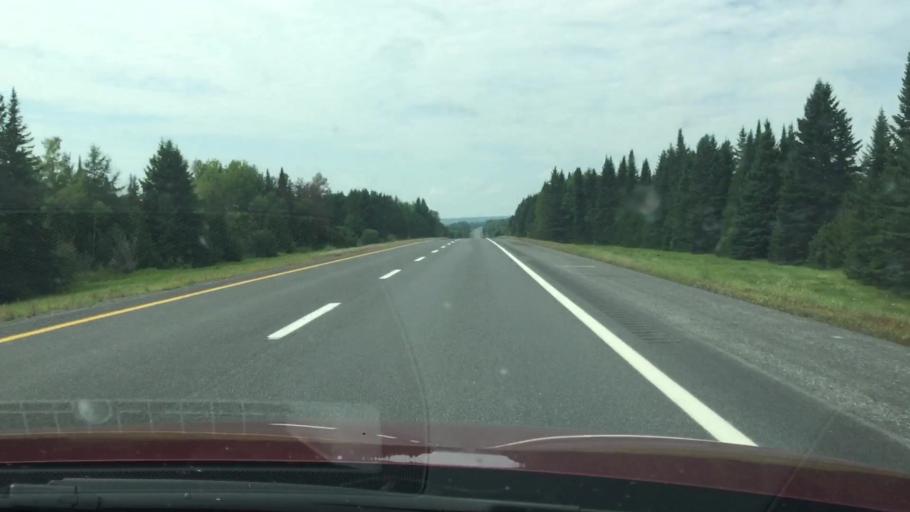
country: US
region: Maine
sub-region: Aroostook County
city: Houlton
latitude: 46.1413
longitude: -67.9710
